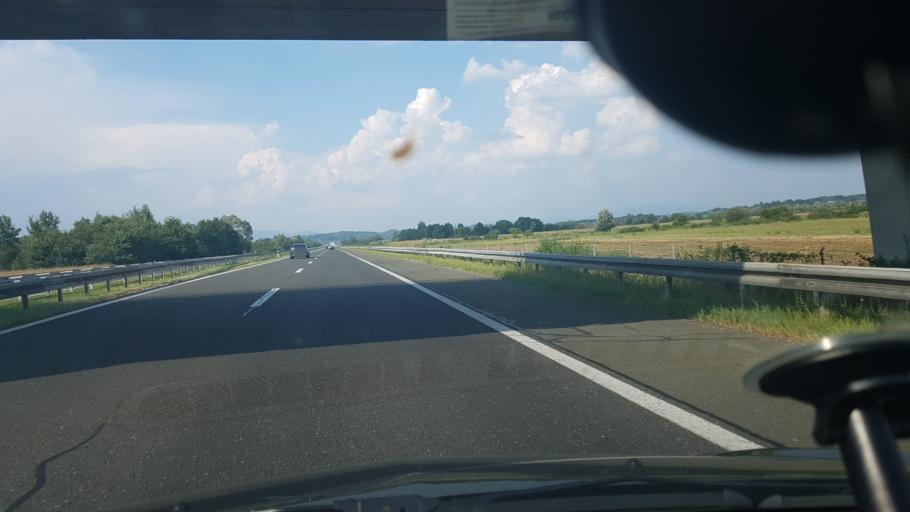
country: HR
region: Zagrebacka
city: Jakovlje
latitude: 45.9746
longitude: 15.8539
